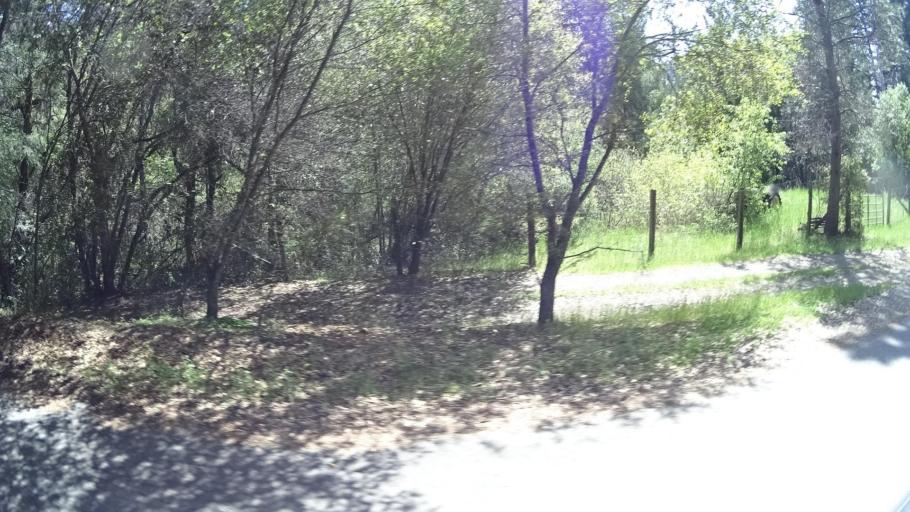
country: US
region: California
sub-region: Humboldt County
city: Redway
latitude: 40.1962
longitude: -123.5575
